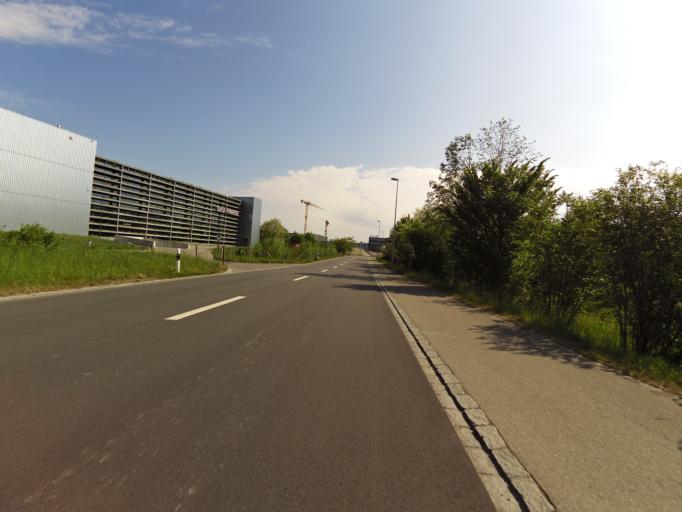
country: CH
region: Thurgau
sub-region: Frauenfeld District
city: Frauenfeld
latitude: 47.5723
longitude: 8.9153
